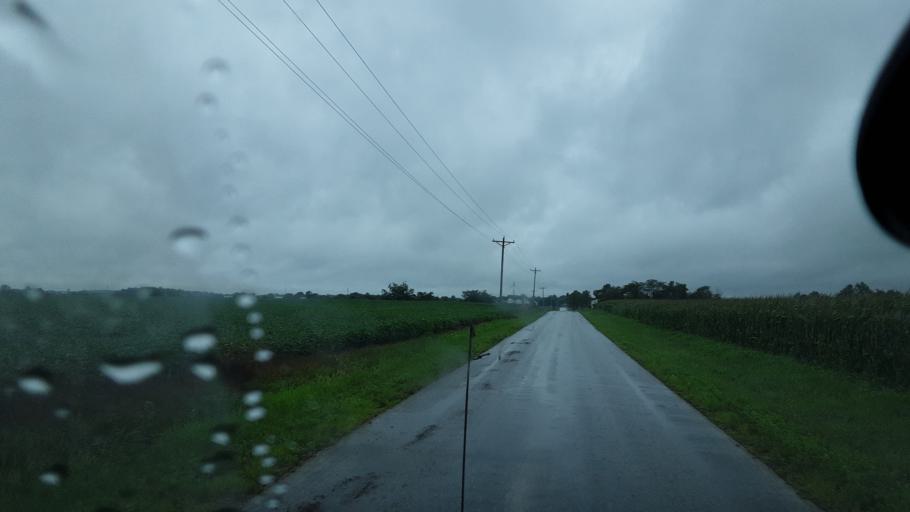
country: US
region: Indiana
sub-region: Adams County
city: Decatur
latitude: 40.7651
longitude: -84.8607
